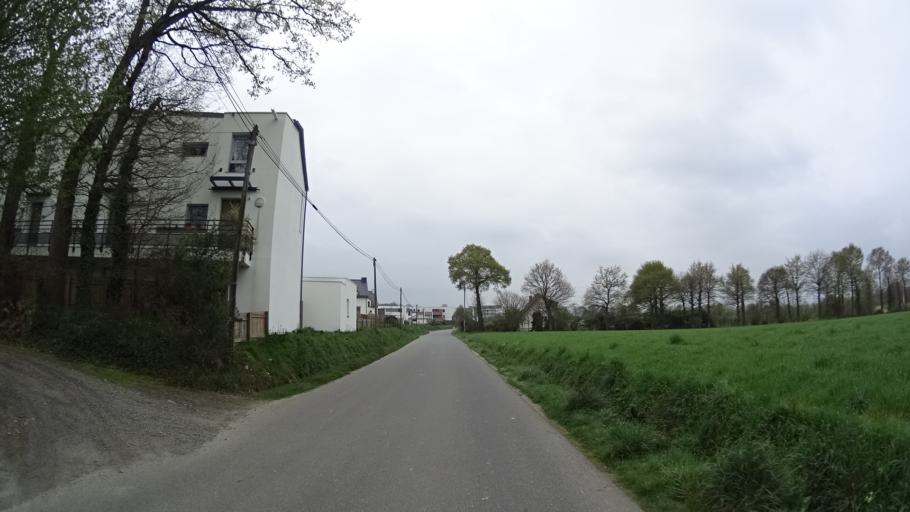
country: FR
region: Brittany
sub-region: Departement d'Ille-et-Vilaine
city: Saint-Gilles
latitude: 48.1509
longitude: -1.8424
